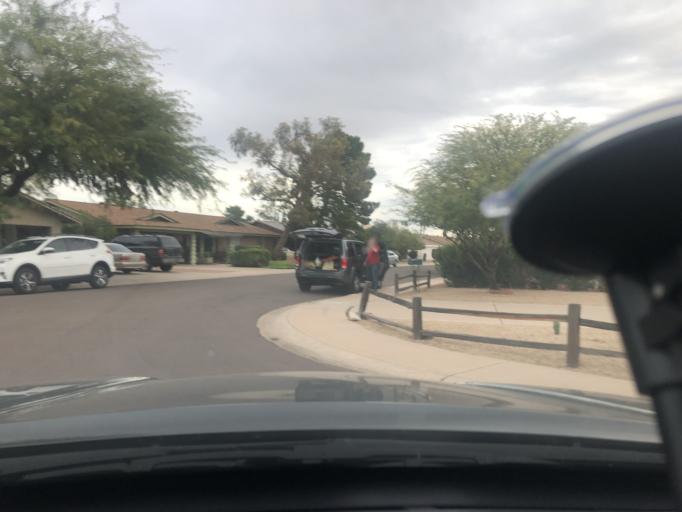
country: US
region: Arizona
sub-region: Maricopa County
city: Scottsdale
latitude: 33.4864
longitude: -111.8992
